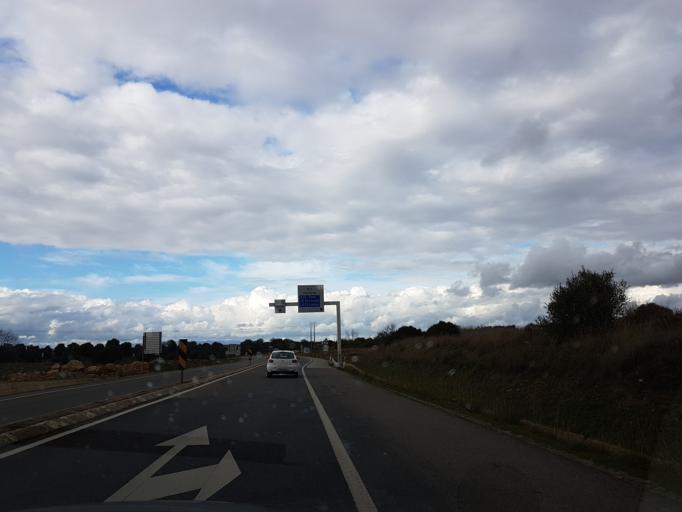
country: PT
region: Faro
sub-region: Albufeira
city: Ferreiras
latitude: 37.1260
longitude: -8.2548
